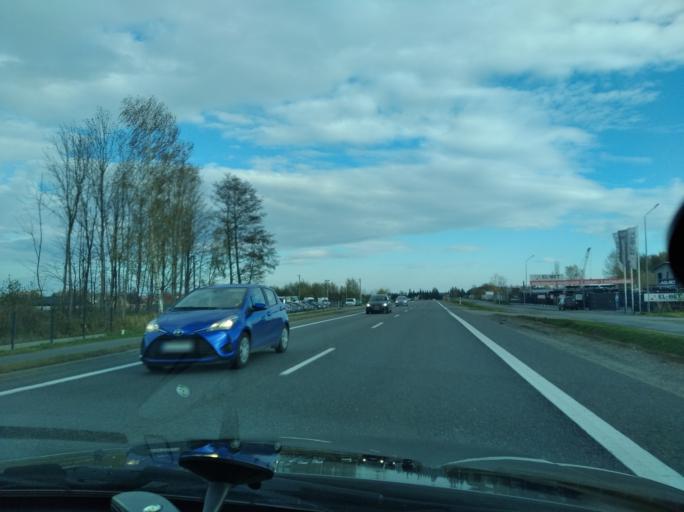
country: PL
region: Subcarpathian Voivodeship
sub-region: Powiat debicki
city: Debica
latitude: 50.0493
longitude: 21.4455
